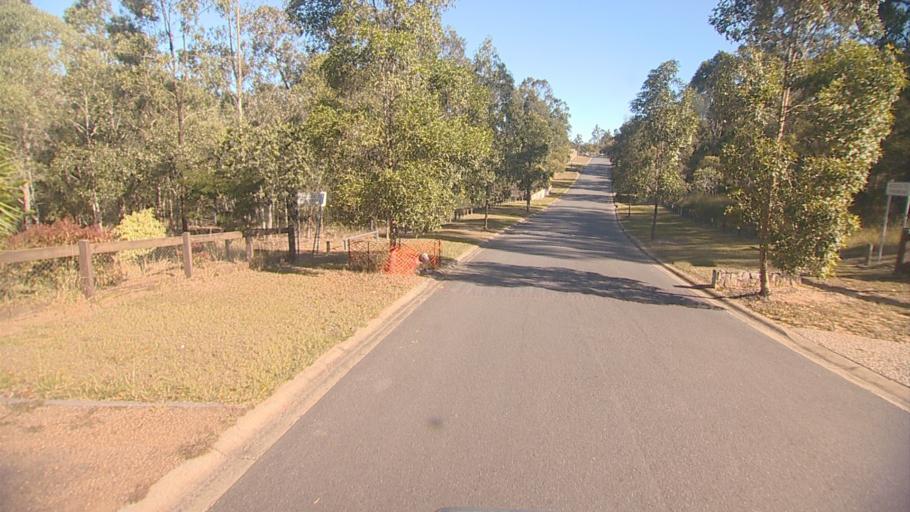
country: AU
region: Queensland
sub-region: Ipswich
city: Springfield Lakes
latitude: -27.7245
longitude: 152.9243
